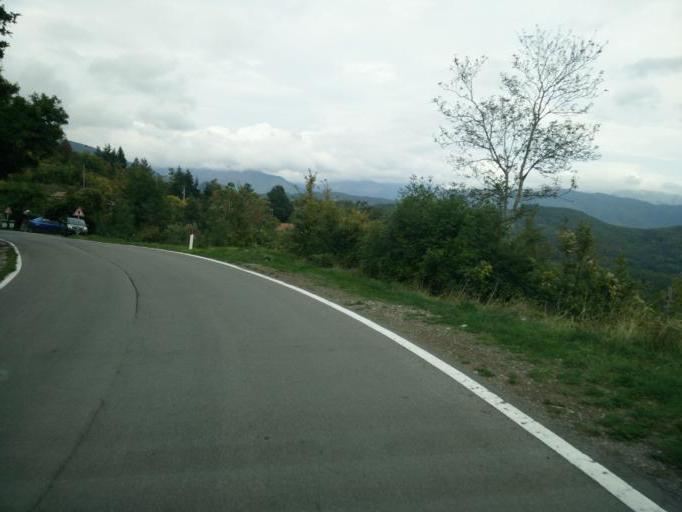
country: IT
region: Tuscany
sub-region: Provincia di Lucca
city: Giuncugnano
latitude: 44.2030
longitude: 10.2394
